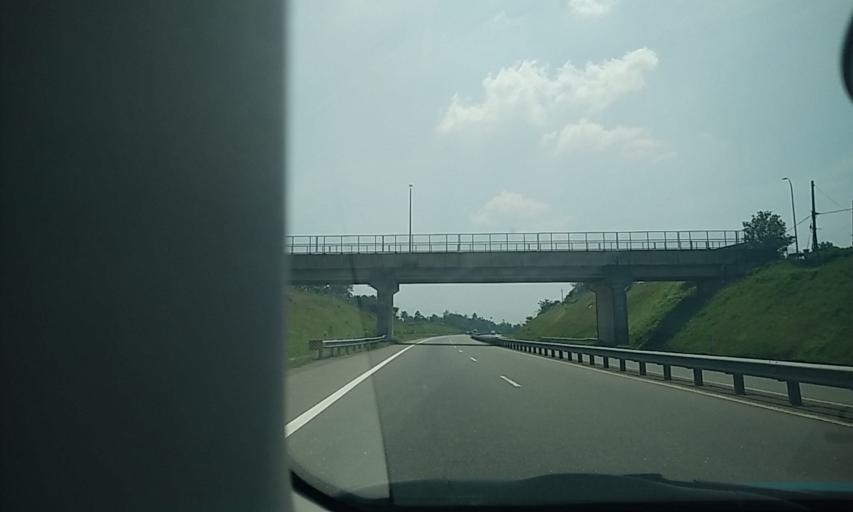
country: LK
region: Western
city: Horana South
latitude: 6.7496
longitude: 79.9965
